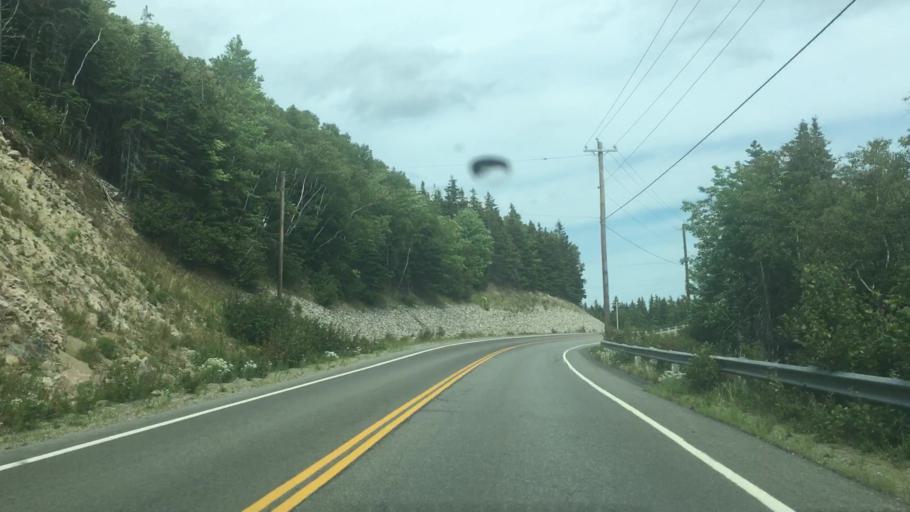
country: CA
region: Nova Scotia
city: Sydney Mines
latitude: 46.5340
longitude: -60.4162
